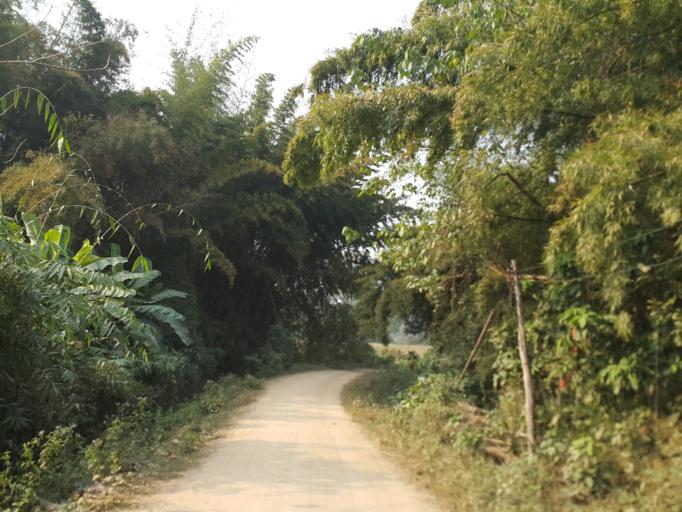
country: TH
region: Lamphun
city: Li
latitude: 17.6077
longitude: 98.9635
